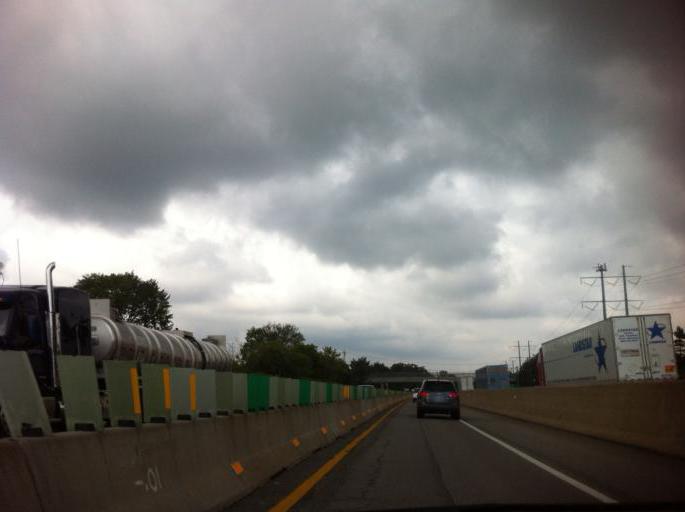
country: US
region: Ohio
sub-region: Cuyahoga County
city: North Royalton
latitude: 41.3176
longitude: -81.7713
